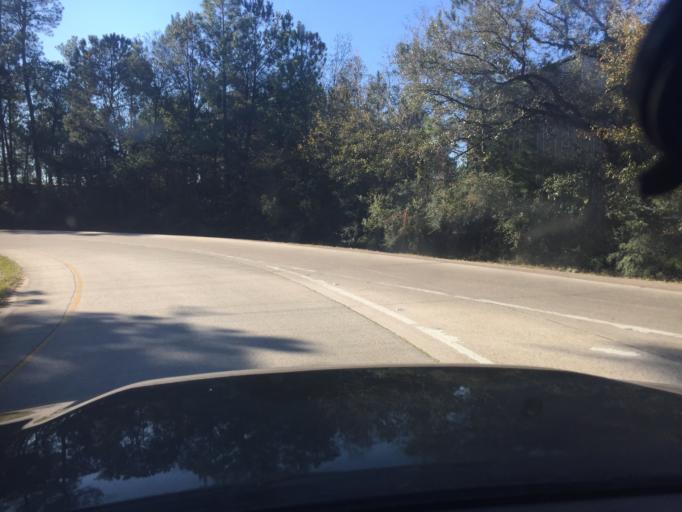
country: US
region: Louisiana
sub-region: Saint Tammany Parish
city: Pearl River
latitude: 30.3542
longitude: -89.7428
